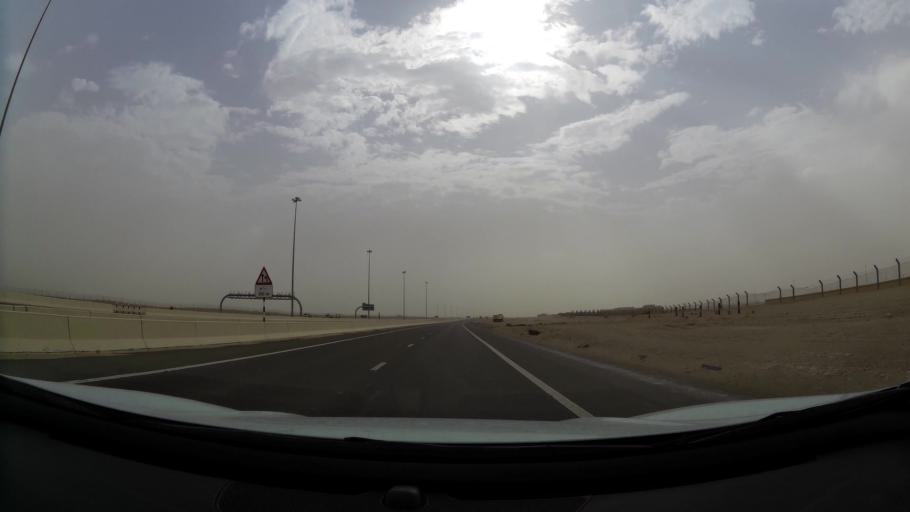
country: AE
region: Abu Dhabi
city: Abu Dhabi
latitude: 24.4801
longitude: 54.6599
